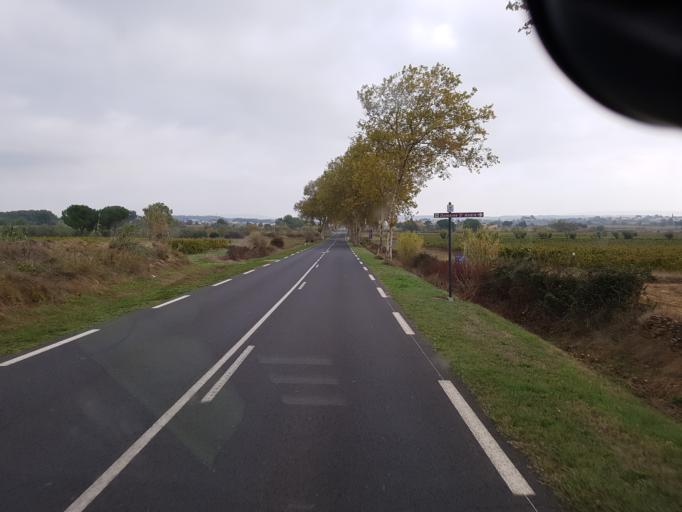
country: FR
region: Languedoc-Roussillon
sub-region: Departement de l'Herault
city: Meze
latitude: 43.4320
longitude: 3.5675
